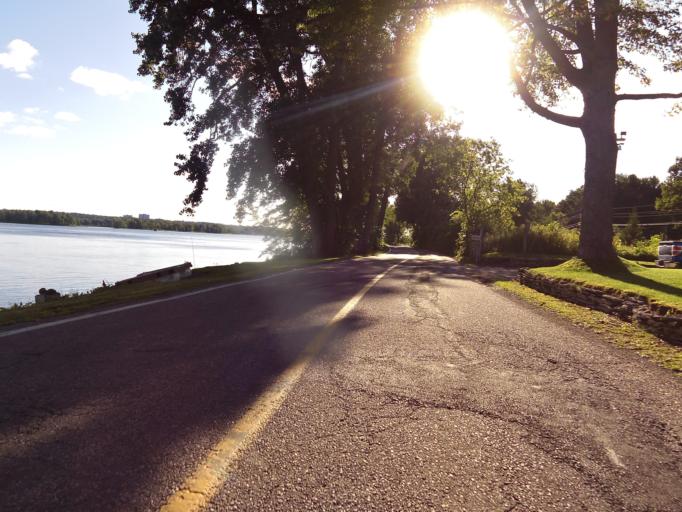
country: CA
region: Quebec
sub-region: Outaouais
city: Gatineau
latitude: 45.4783
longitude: -75.5880
